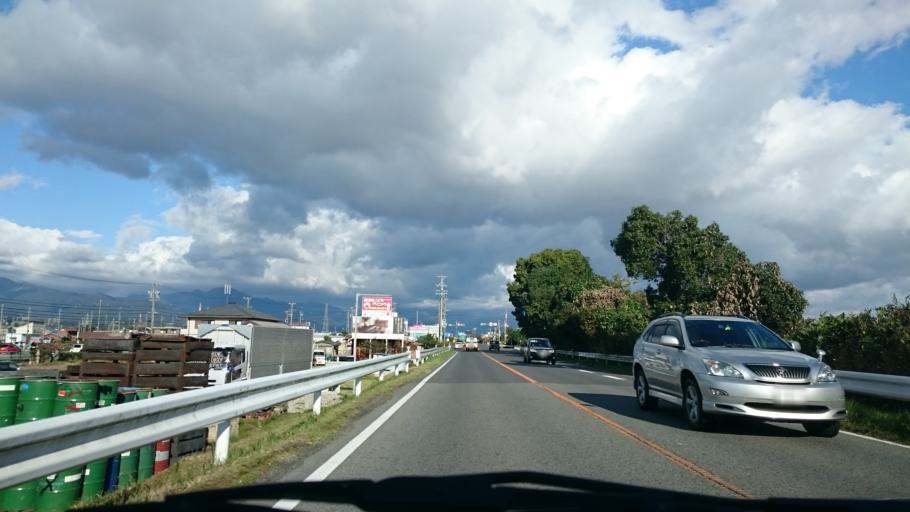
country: JP
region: Mie
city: Komono
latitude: 34.9833
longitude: 136.5560
